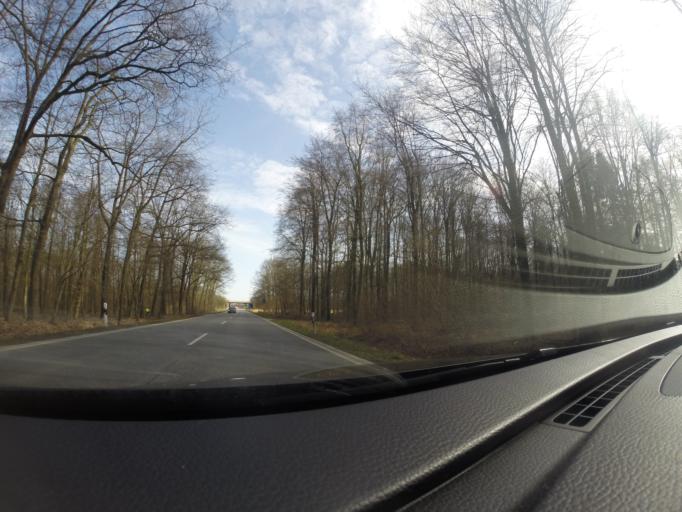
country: DE
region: North Rhine-Westphalia
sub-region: Regierungsbezirk Munster
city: Legden
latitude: 52.0523
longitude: 7.0583
